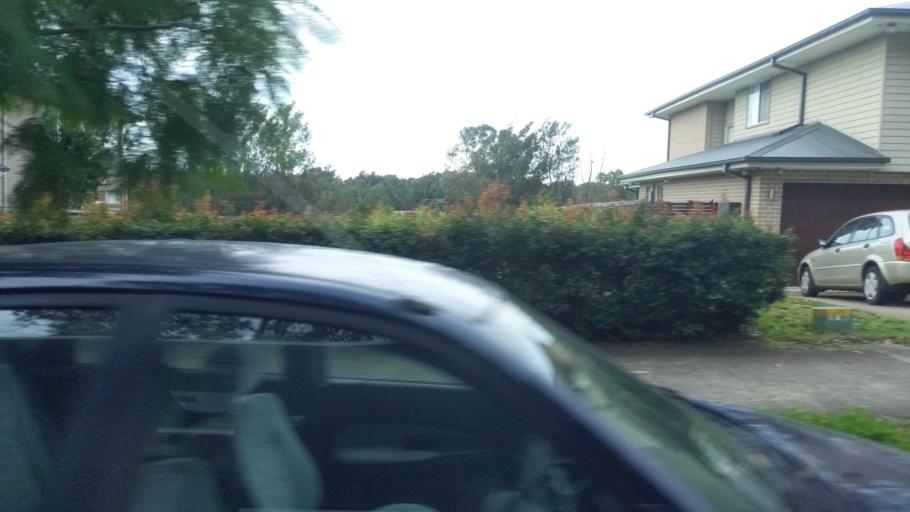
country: AU
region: New South Wales
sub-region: Blacktown
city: Quakers Hill
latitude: -33.7290
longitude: 150.8658
